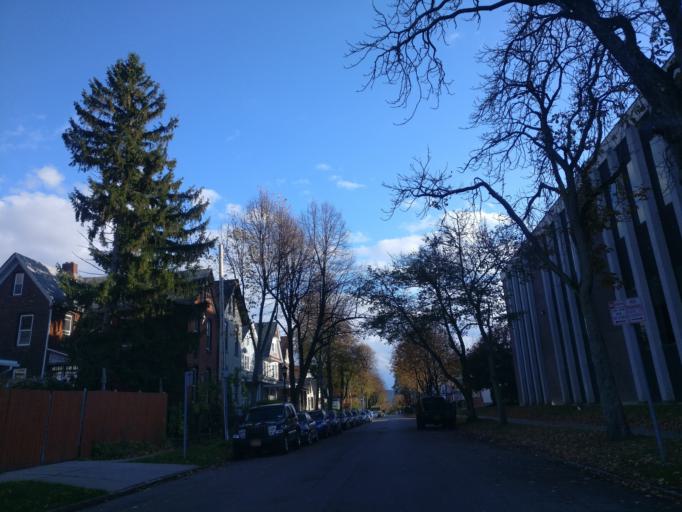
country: US
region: New York
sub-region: Erie County
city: Buffalo
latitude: 42.9024
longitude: -78.8897
